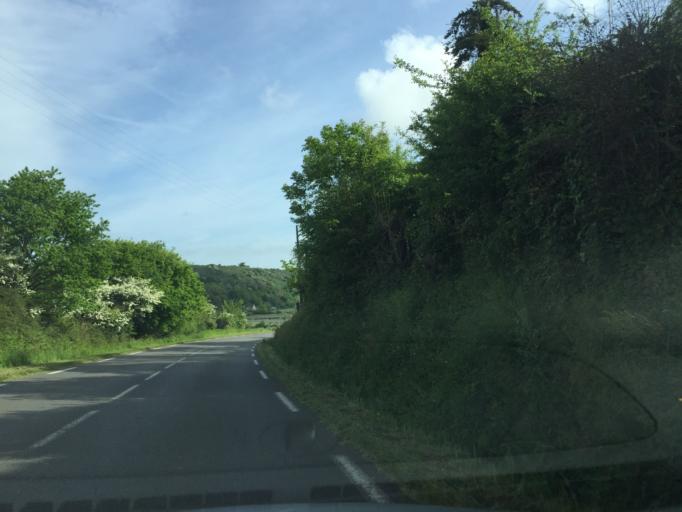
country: FR
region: Brittany
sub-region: Departement des Cotes-d'Armor
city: Matignon
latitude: 48.6158
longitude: -2.3380
